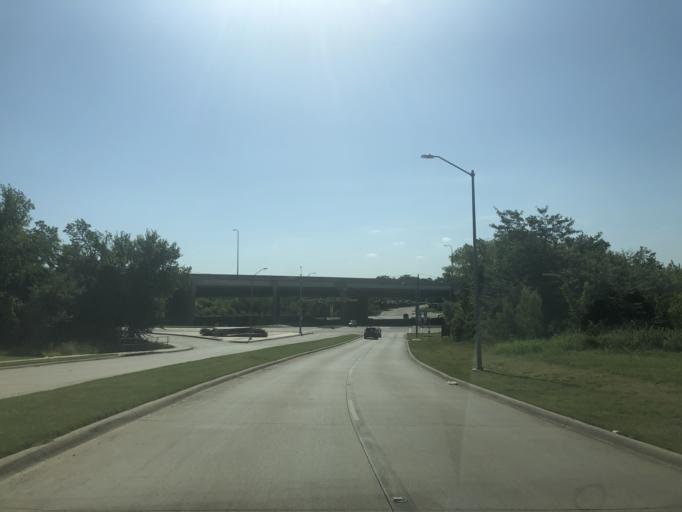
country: US
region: Texas
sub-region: Dallas County
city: Grand Prairie
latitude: 32.7509
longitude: -97.0305
